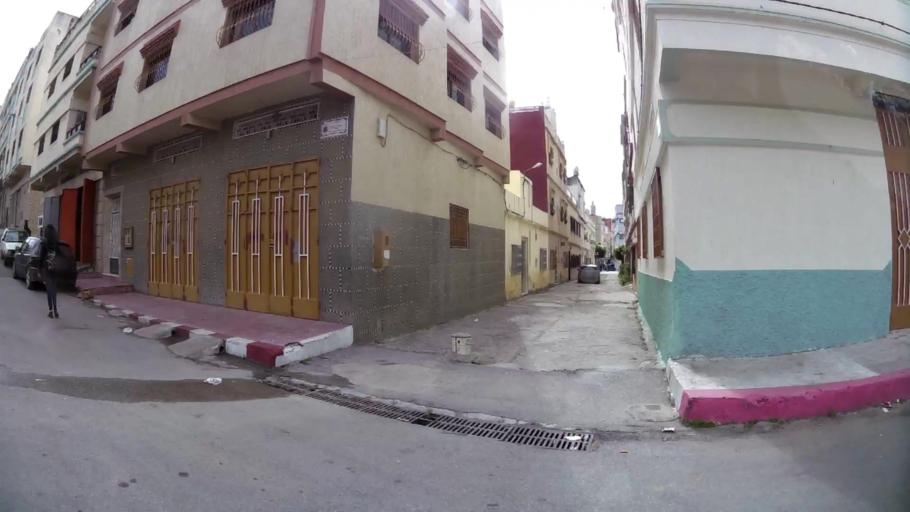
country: MA
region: Tanger-Tetouan
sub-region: Tanger-Assilah
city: Tangier
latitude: 35.7601
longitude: -5.7998
